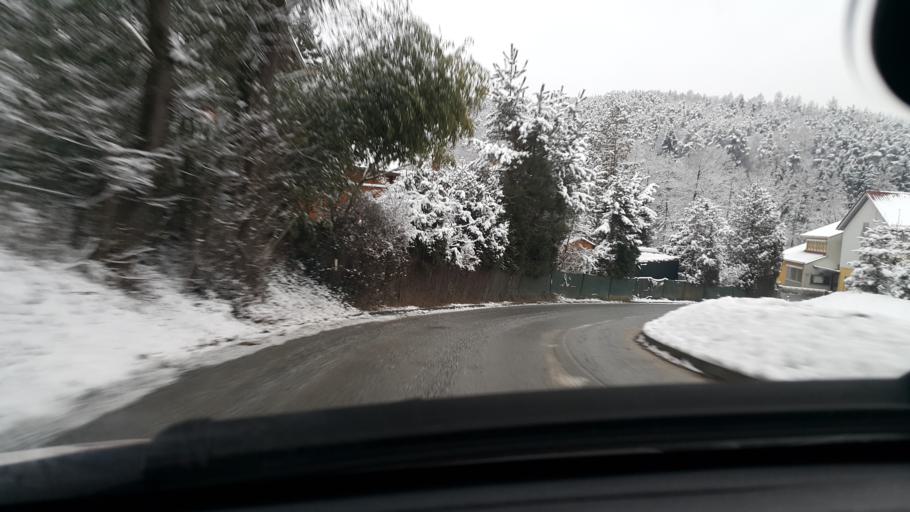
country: AT
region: Styria
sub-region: Politischer Bezirk Graz-Umgebung
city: Hitzendorf
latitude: 47.0633
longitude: 15.2959
